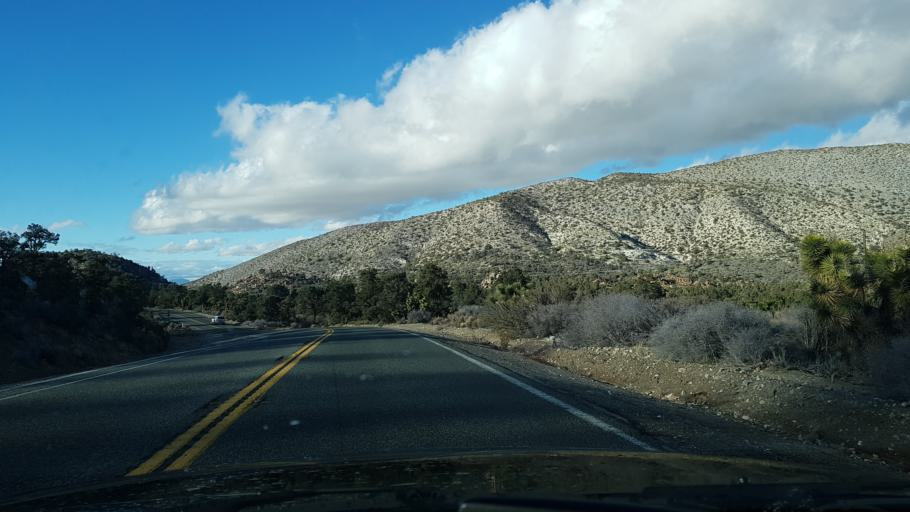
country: US
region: California
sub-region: San Bernardino County
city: Big Bear City
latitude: 34.3211
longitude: -116.8178
